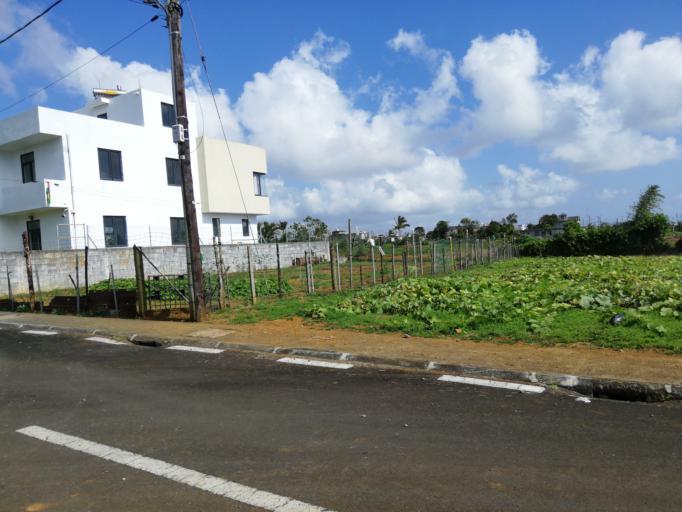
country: MU
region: Moka
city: Verdun
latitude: -20.2151
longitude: 57.5498
